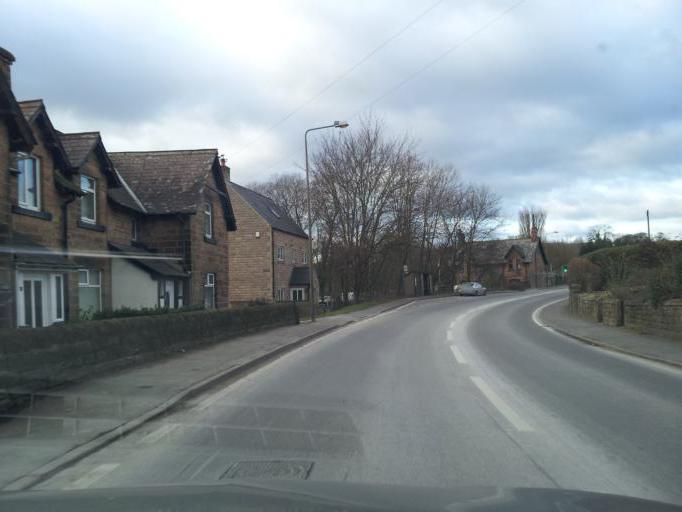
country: GB
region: England
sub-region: Derbyshire
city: Matlock
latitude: 53.1765
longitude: -1.6091
